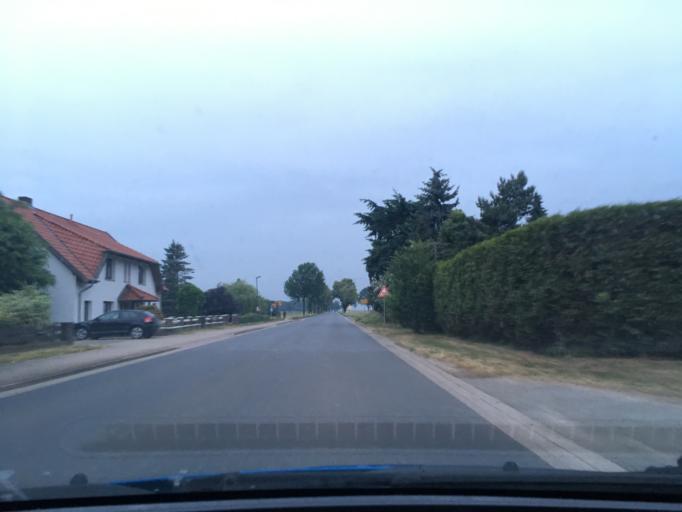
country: DE
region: Lower Saxony
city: Lubbow
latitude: 52.9152
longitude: 11.1802
